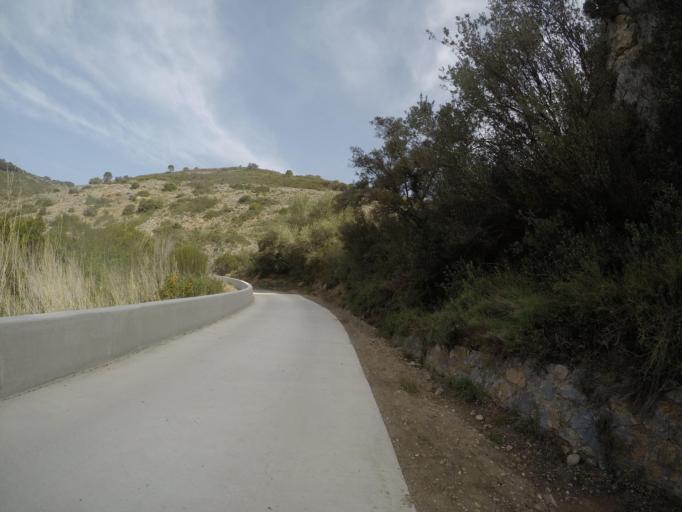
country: FR
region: Languedoc-Roussillon
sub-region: Departement des Pyrenees-Orientales
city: Estagel
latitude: 42.7798
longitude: 2.7253
